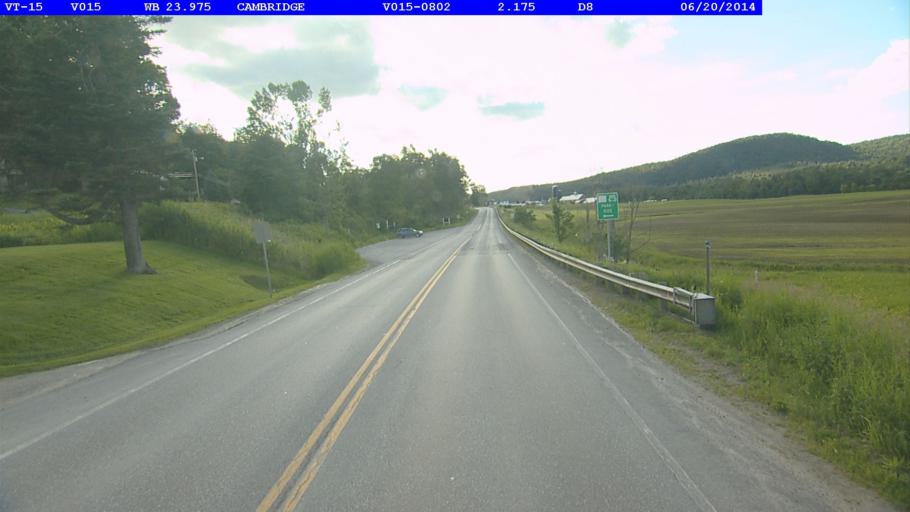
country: US
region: Vermont
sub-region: Chittenden County
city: Jericho
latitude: 44.6455
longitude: -72.8824
